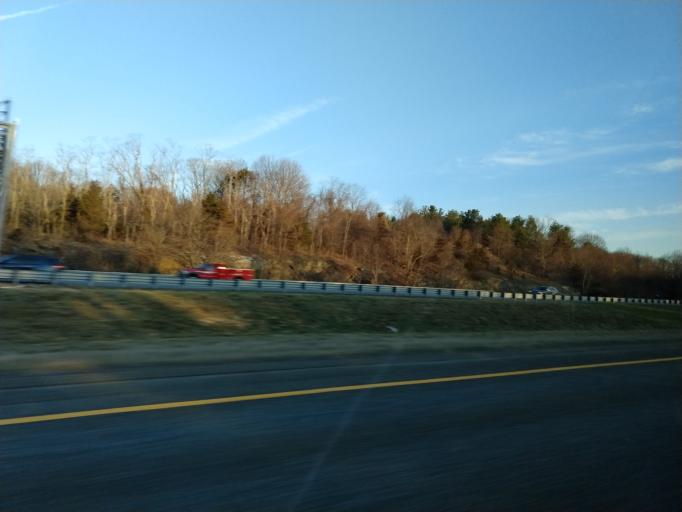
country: US
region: Massachusetts
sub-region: Essex County
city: Danvers
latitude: 42.5668
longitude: -70.9709
